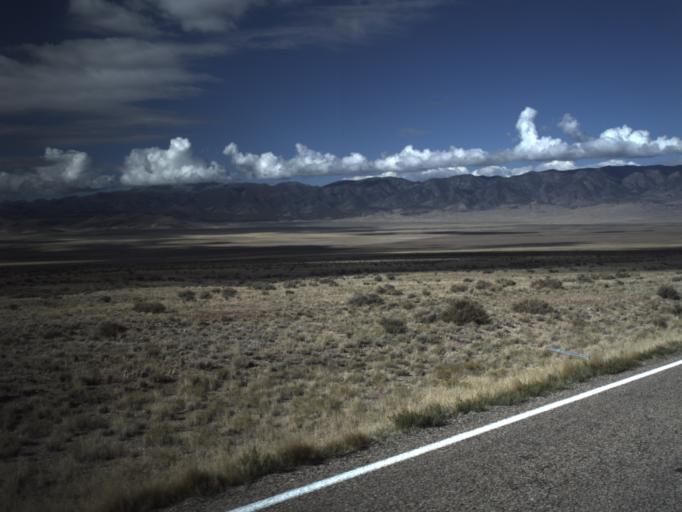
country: US
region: Utah
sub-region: Beaver County
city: Milford
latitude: 38.4405
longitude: -113.3170
